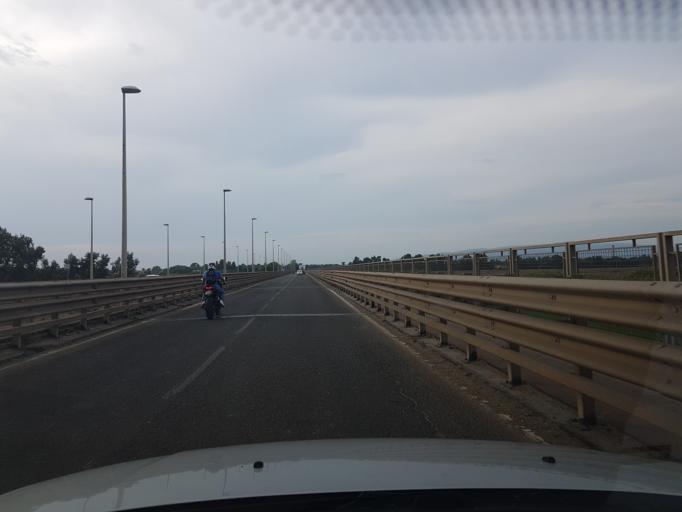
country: IT
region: Sardinia
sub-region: Provincia di Oristano
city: Donigala Fenugheddu
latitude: 39.9181
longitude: 8.5838
